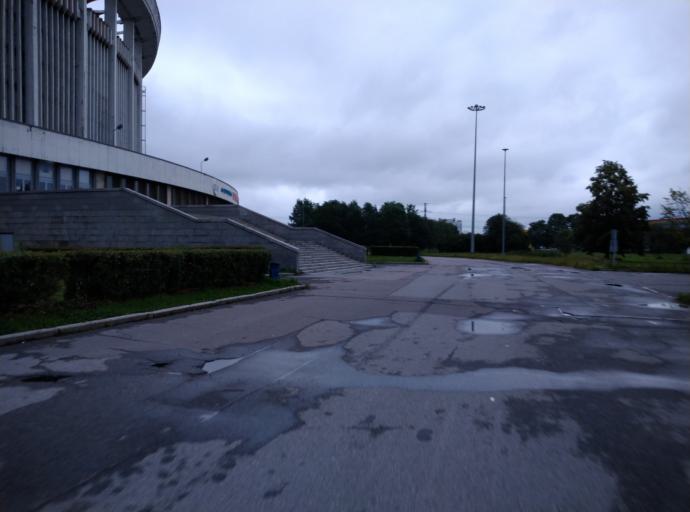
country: RU
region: St.-Petersburg
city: Kupchino
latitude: 59.8681
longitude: 30.3414
